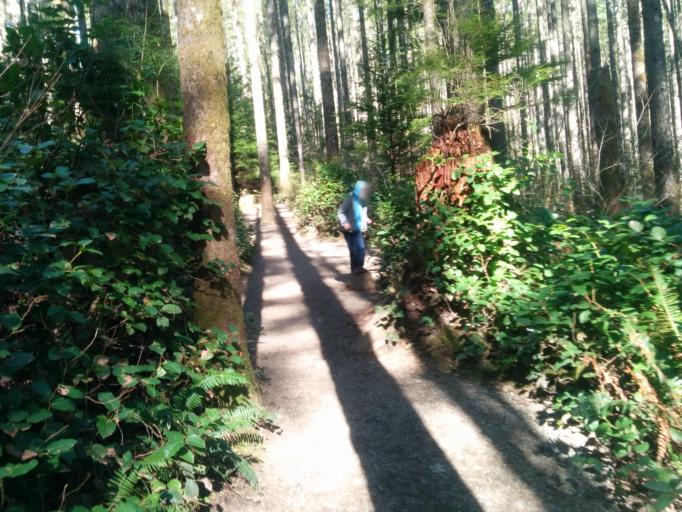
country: US
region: Washington
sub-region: King County
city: Riverbend
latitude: 47.4358
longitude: -121.7730
